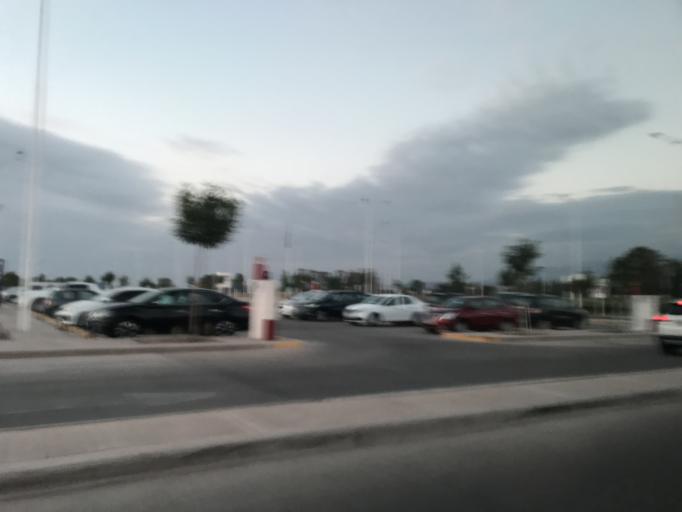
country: AR
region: Mendoza
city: Las Heras
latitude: -32.8269
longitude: -68.7998
